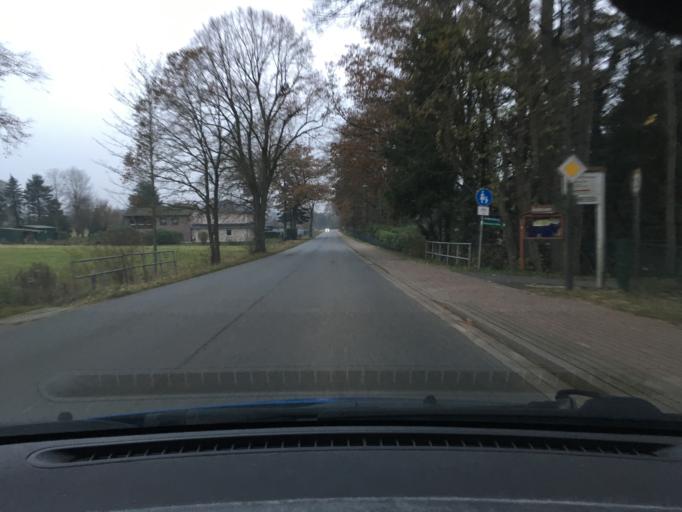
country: DE
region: Lower Saxony
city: Bispingen
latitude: 53.1065
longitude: 9.9685
